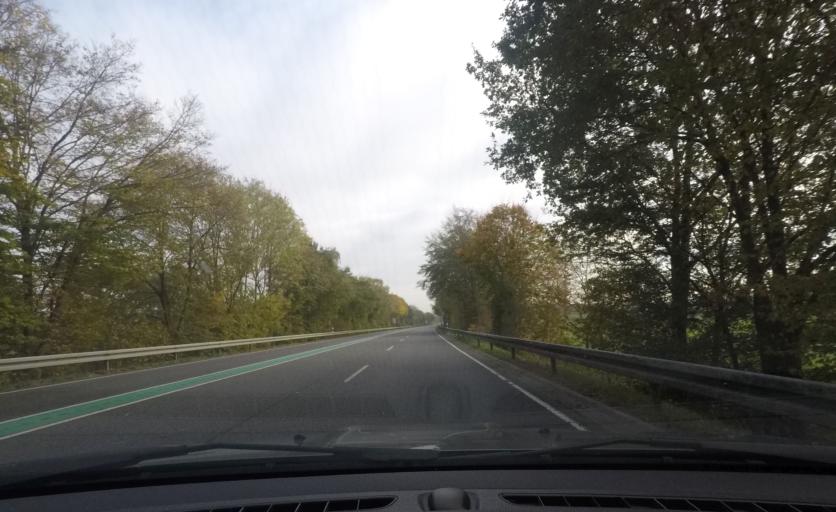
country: DE
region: North Rhine-Westphalia
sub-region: Regierungsbezirk Munster
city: Klein Reken
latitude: 51.8541
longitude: 7.0635
